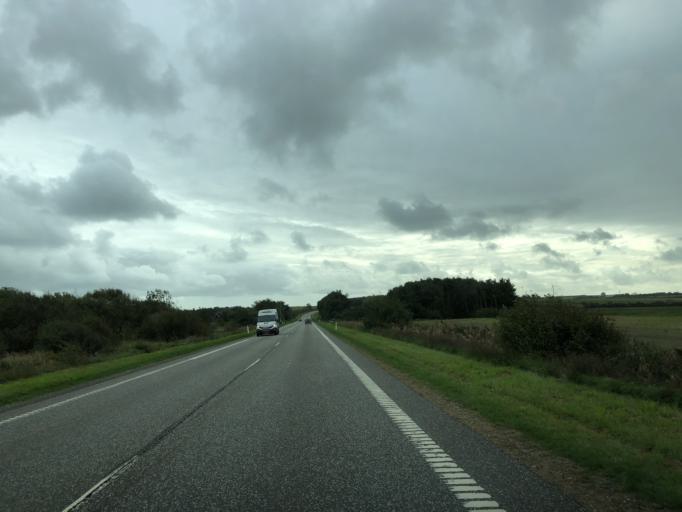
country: DK
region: North Denmark
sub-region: Thisted Kommune
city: Hurup
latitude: 56.7855
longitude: 8.4675
